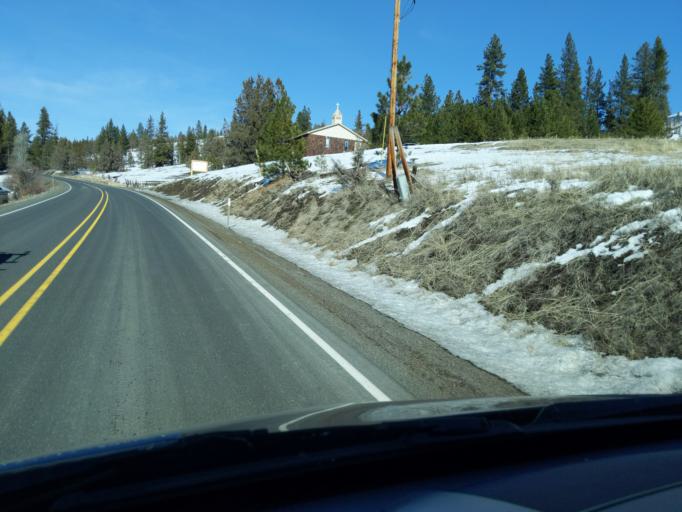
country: US
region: Oregon
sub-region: Grant County
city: John Day
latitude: 44.8795
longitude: -119.0151
